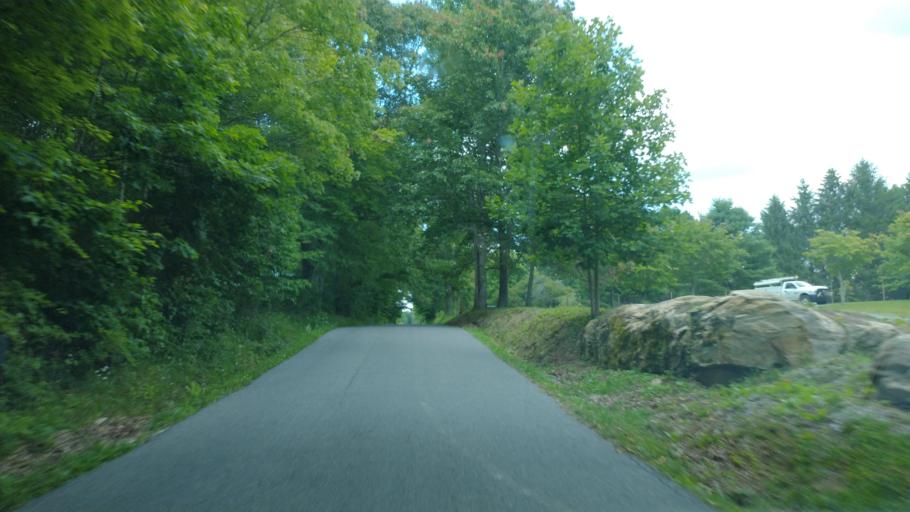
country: US
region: West Virginia
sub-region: Mercer County
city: Athens
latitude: 37.4577
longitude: -81.0429
